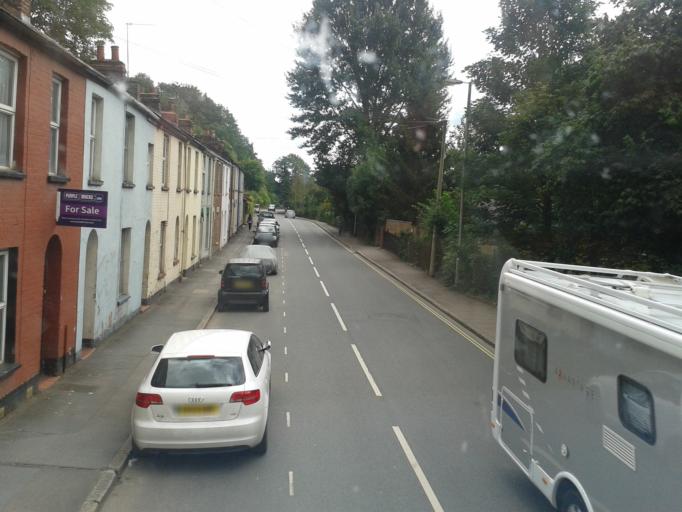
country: GB
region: England
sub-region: Devon
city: Exeter
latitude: 50.7254
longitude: -3.5401
